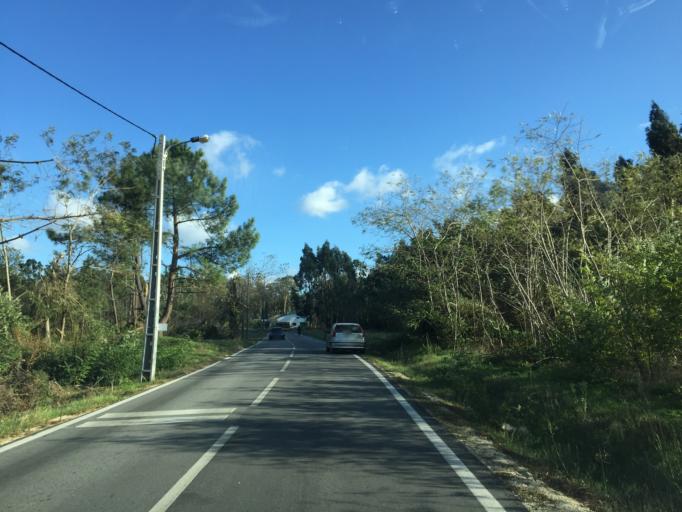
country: PT
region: Coimbra
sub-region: Figueira da Foz
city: Tavarede
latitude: 40.2081
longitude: -8.8413
